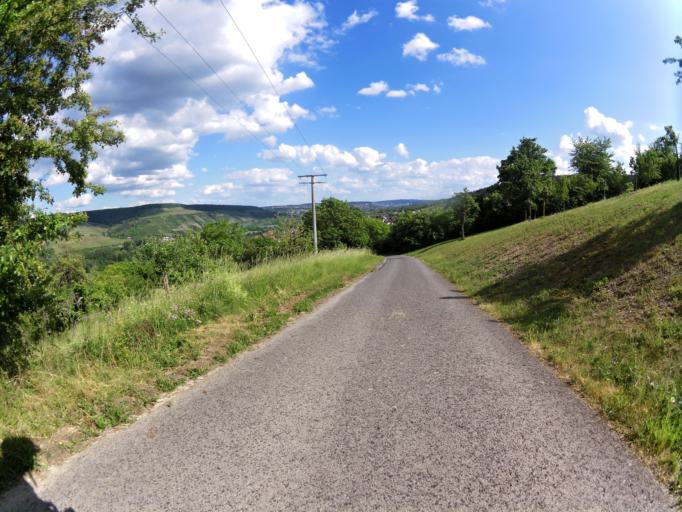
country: DE
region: Bavaria
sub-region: Regierungsbezirk Unterfranken
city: Erlabrunn
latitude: 49.8625
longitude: 9.8363
